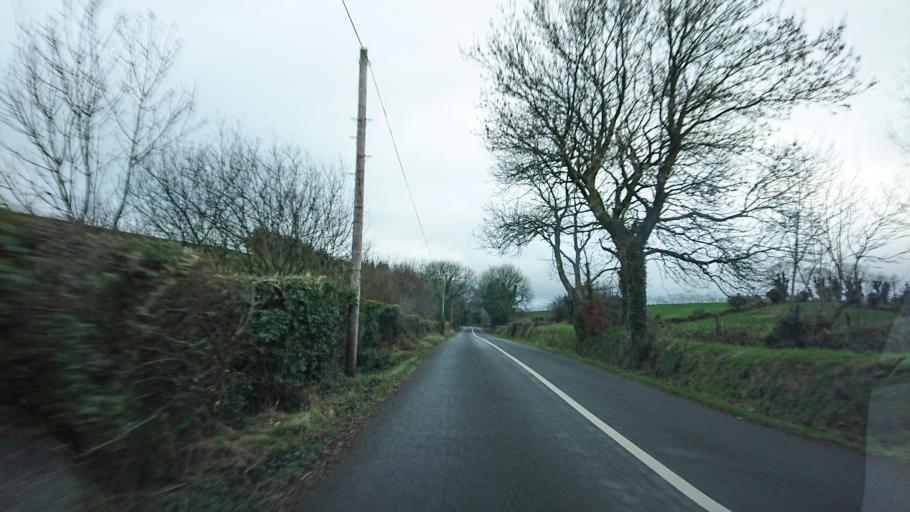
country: IE
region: Munster
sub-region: Waterford
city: Portlaw
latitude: 52.2672
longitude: -7.3983
